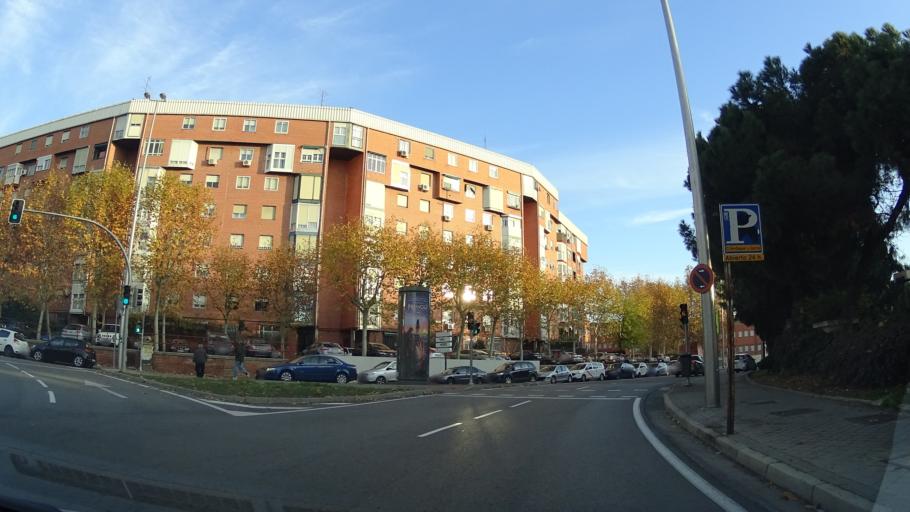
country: ES
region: Madrid
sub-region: Provincia de Madrid
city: Ciudad Lineal
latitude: 40.4406
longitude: -3.6572
